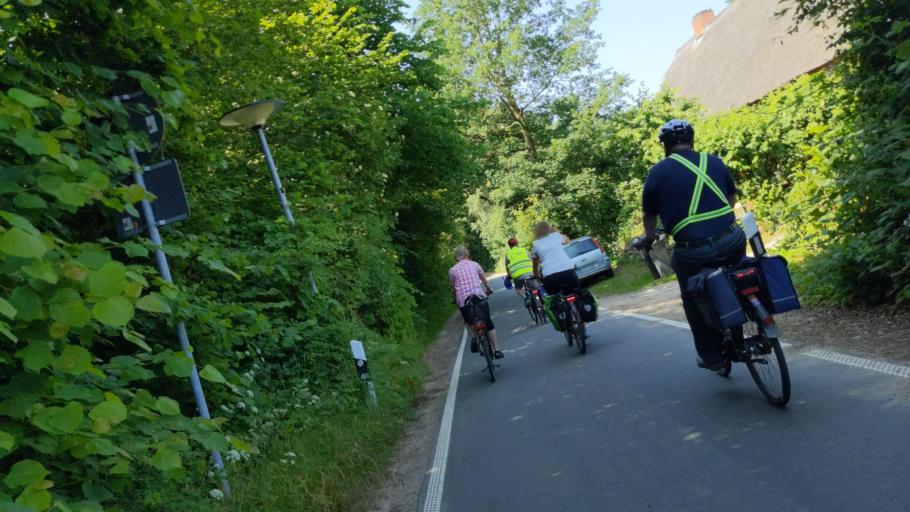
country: DE
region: Schleswig-Holstein
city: Krummesse
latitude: 53.7817
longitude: 10.6332
